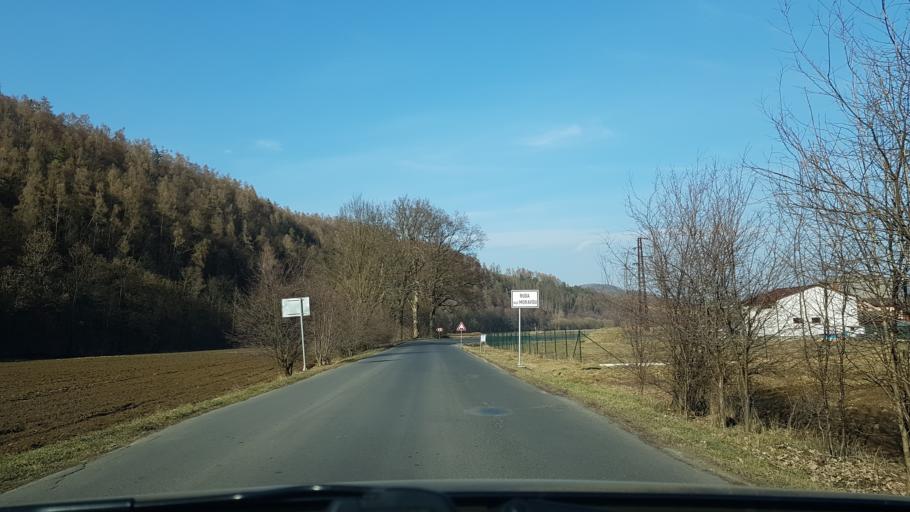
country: CZ
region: Olomoucky
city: Olsany
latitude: 49.9740
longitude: 16.8660
